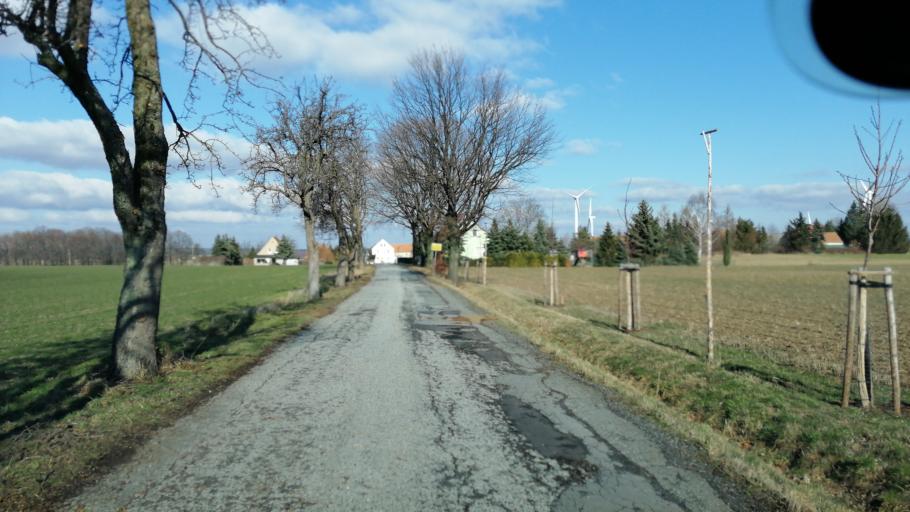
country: DE
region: Saxony
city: Weissenberg
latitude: 51.1758
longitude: 14.7129
